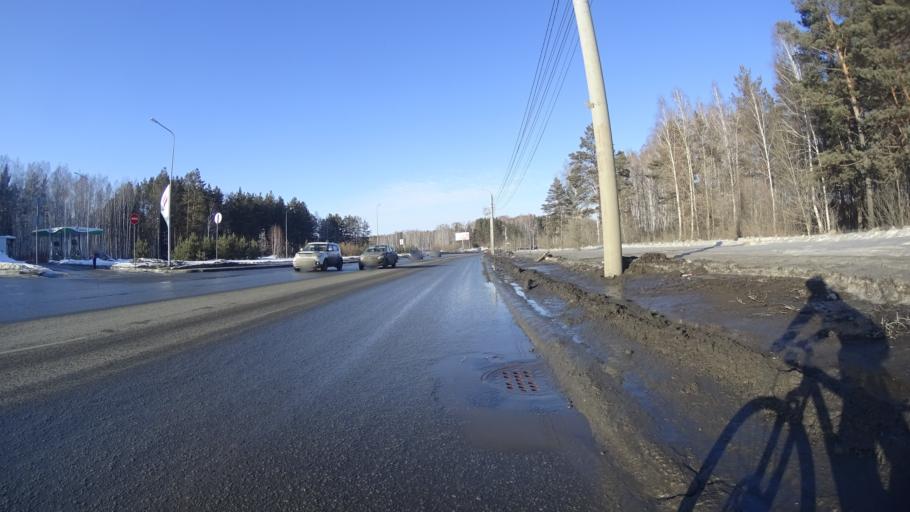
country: RU
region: Chelyabinsk
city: Roshchino
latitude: 55.1982
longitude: 61.2803
